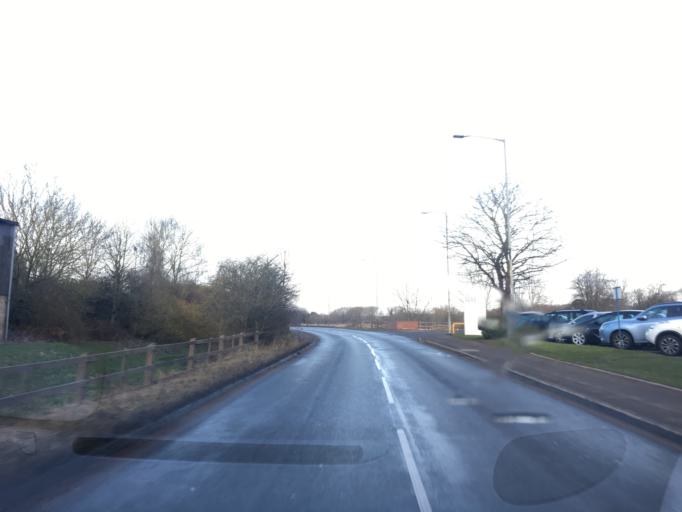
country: GB
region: England
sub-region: Warwickshire
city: Rugby
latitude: 52.3806
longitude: -1.2399
